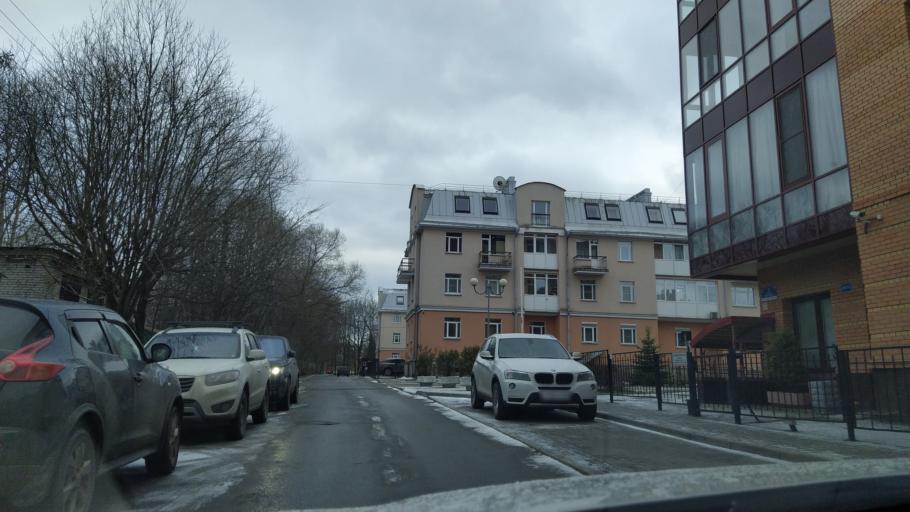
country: RU
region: St.-Petersburg
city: Pushkin
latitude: 59.7289
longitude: 30.4005
